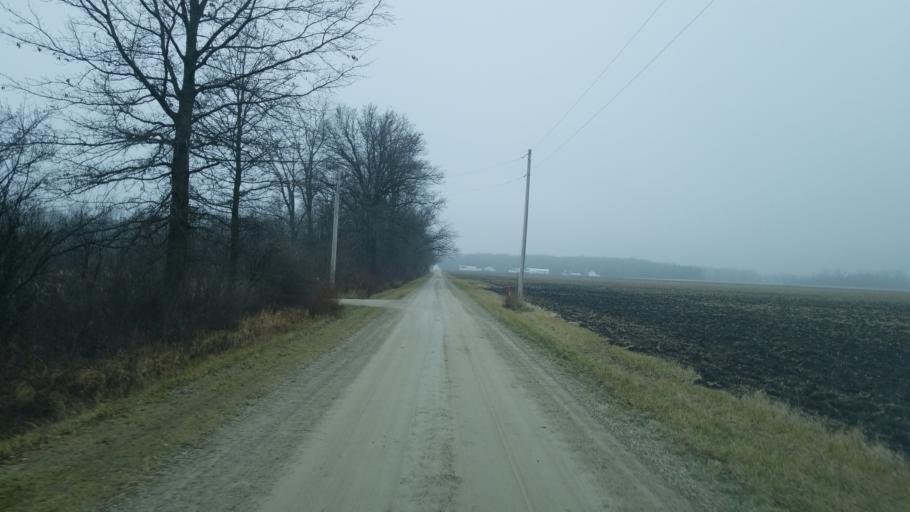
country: US
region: Indiana
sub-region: Adams County
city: Geneva
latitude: 40.5840
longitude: -84.9958
